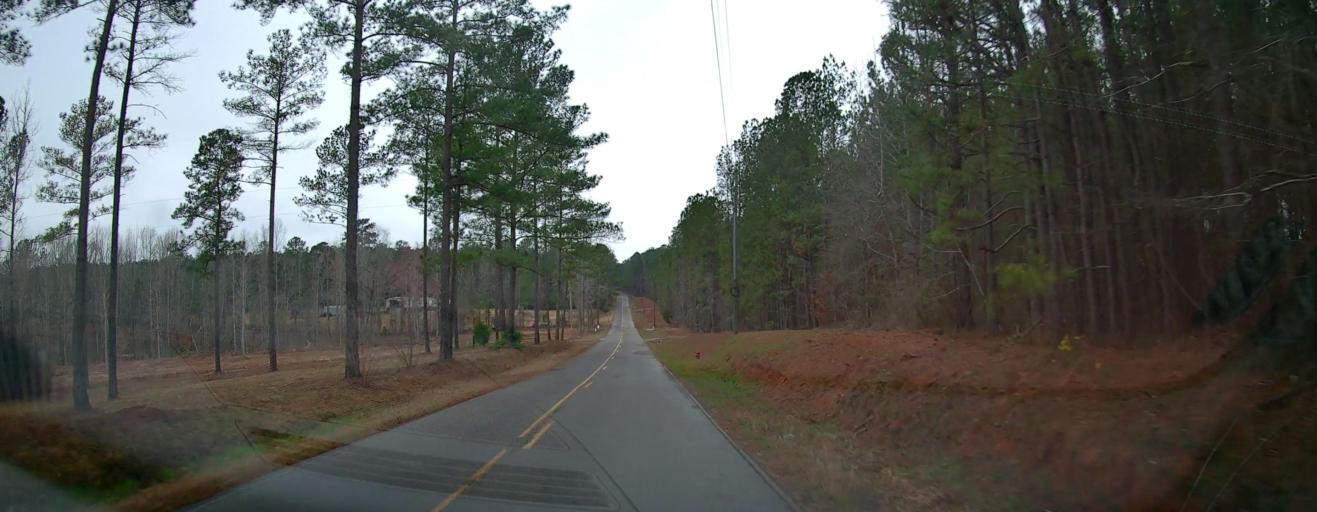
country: US
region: Georgia
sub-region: Monroe County
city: Forsyth
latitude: 33.0171
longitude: -83.8399
